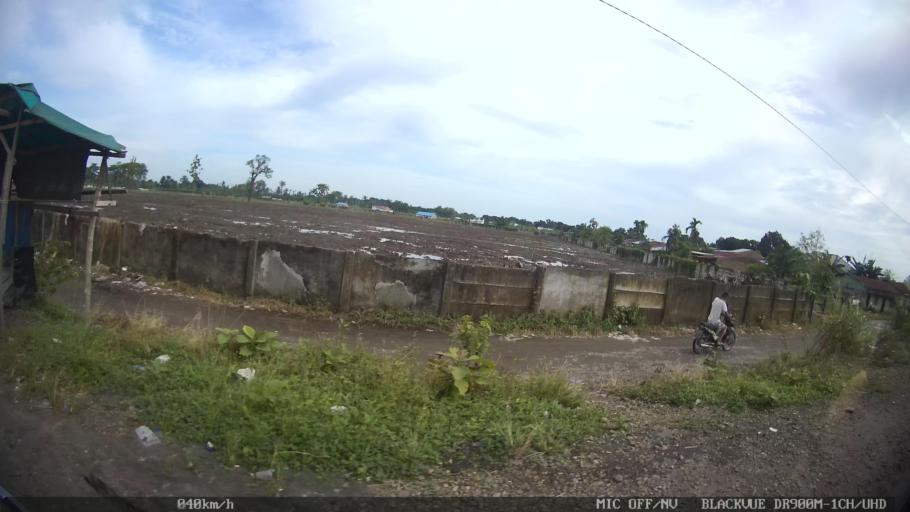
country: ID
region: North Sumatra
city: Medan
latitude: 3.6213
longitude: 98.7182
